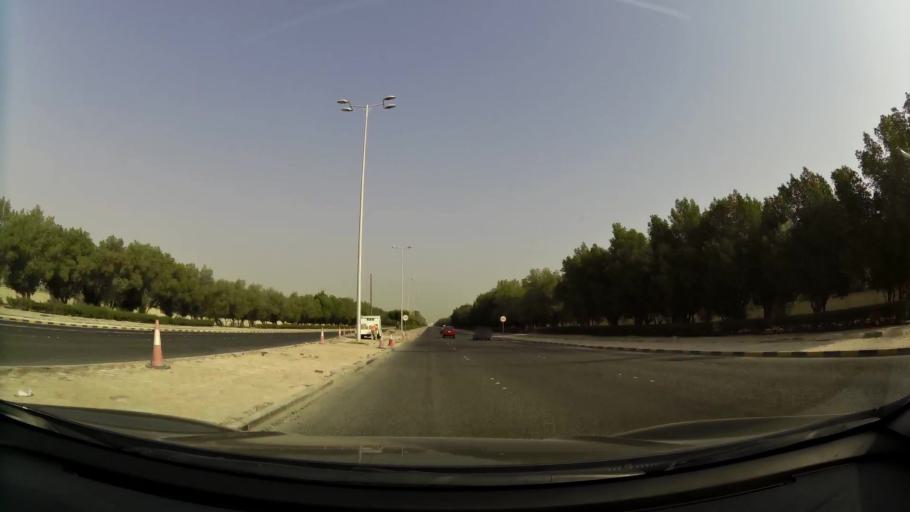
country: KW
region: Al Asimah
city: Ar Rabiyah
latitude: 29.2966
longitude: 47.8322
